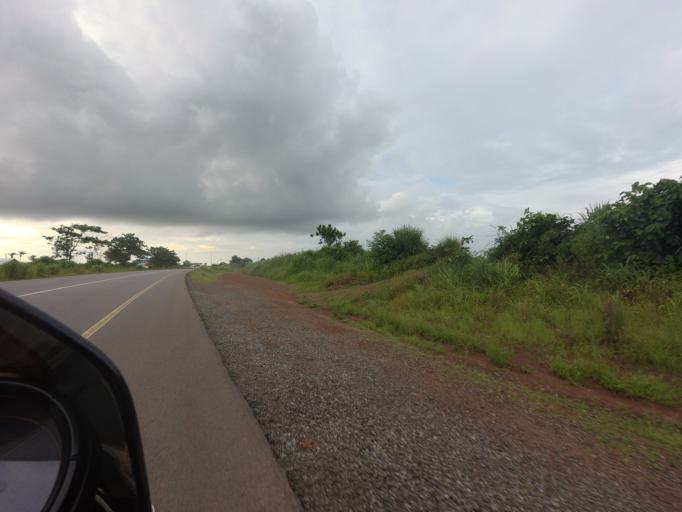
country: SL
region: Northern Province
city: Kambia
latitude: 9.0580
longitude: -12.9166
